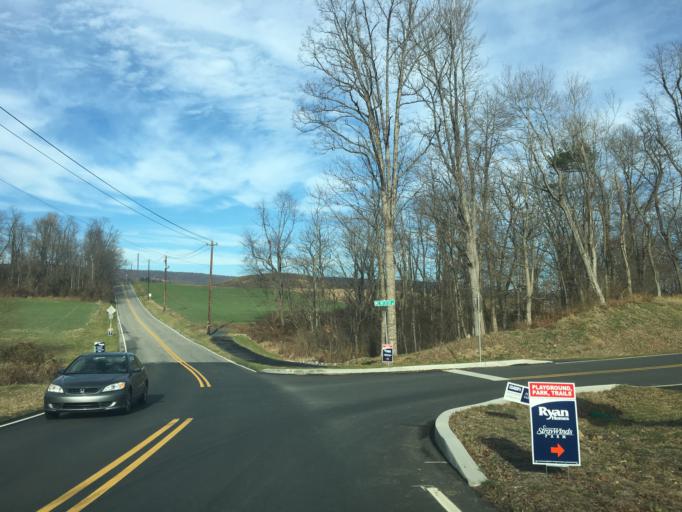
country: US
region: Pennsylvania
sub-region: Dauphin County
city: Colonial Park
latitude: 40.3223
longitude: -76.8414
